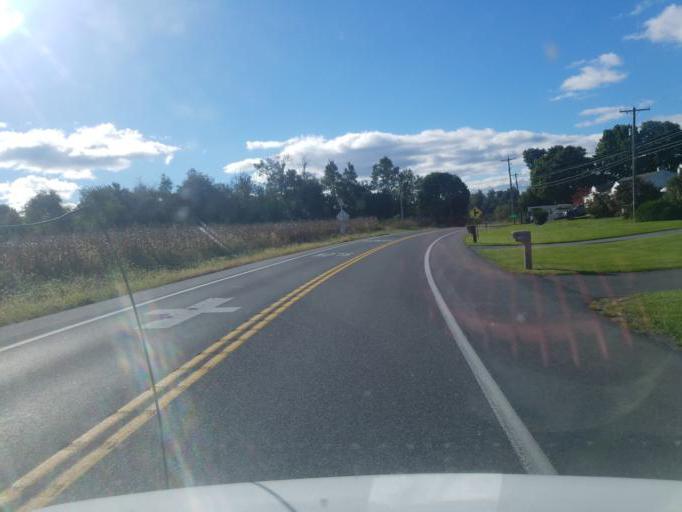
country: US
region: Pennsylvania
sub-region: Franklin County
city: Waynesboro
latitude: 39.7703
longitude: -77.5684
